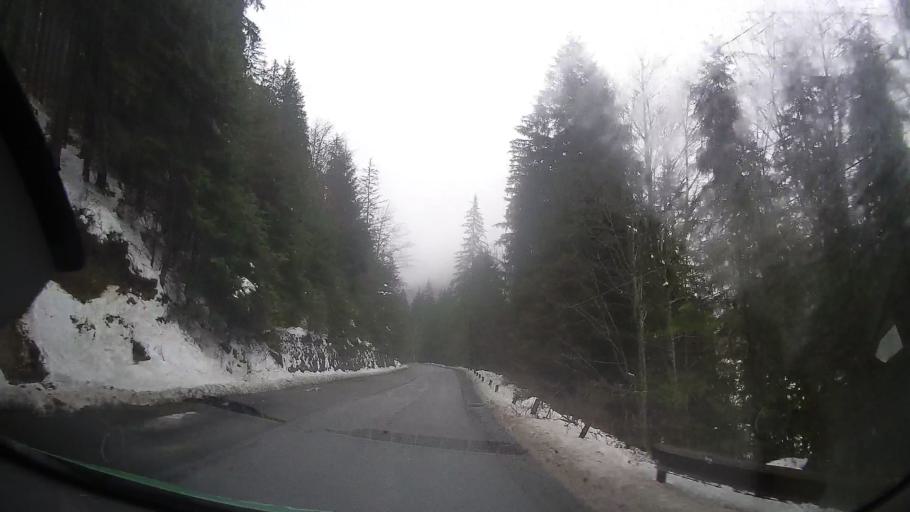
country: RO
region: Neamt
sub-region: Comuna Bicaz Chei
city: Bicaz Chei
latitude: 46.7839
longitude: 25.7868
